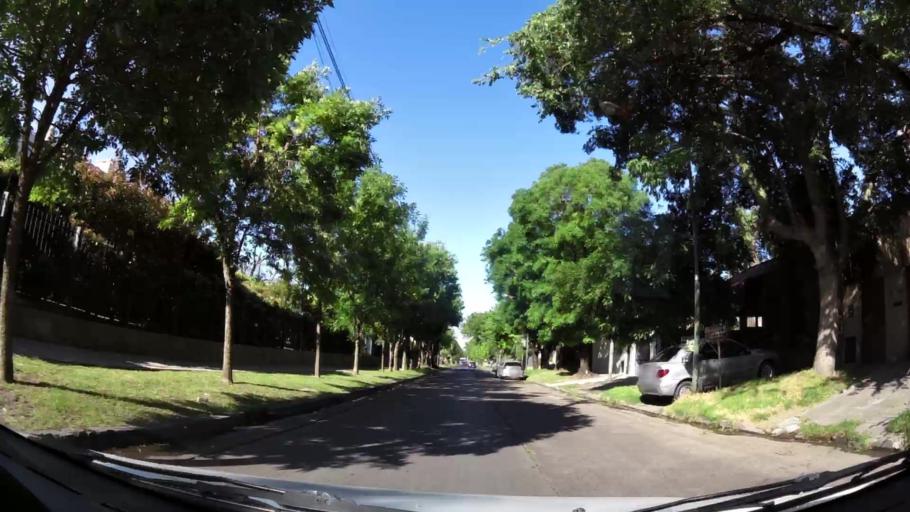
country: AR
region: Buenos Aires
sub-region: Partido de San Isidro
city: San Isidro
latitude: -34.4770
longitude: -58.5338
